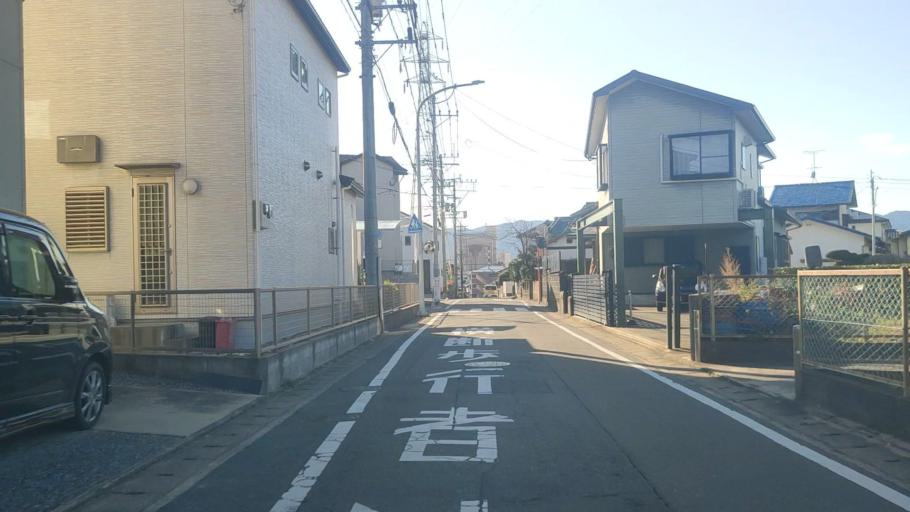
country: JP
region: Fukuoka
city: Fukuoka-shi
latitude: 33.5411
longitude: 130.3521
